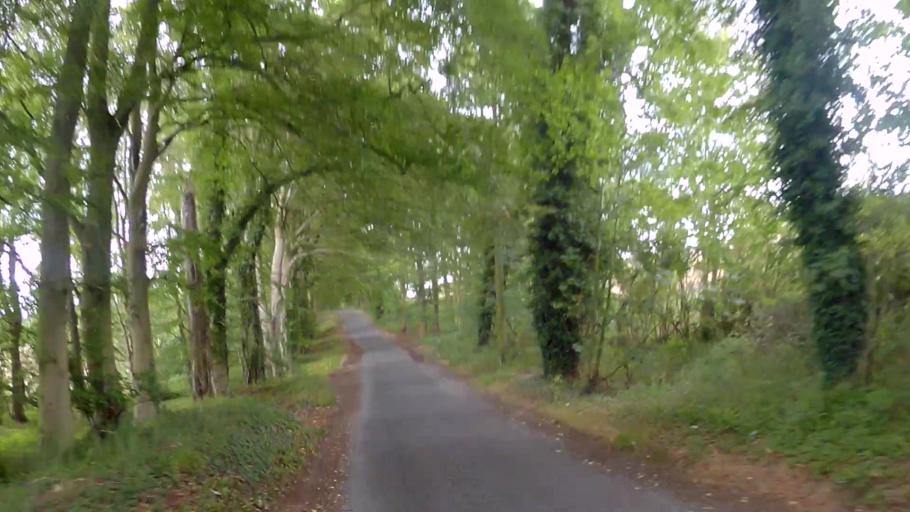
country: GB
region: England
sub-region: Hampshire
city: Overton
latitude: 51.1893
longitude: -1.2776
